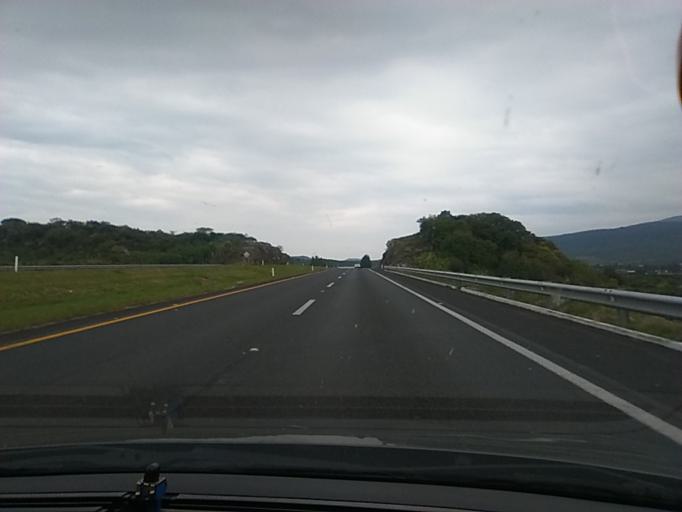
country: MX
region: Michoacan
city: Penjamillo de Degollado
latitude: 20.0243
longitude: -101.9148
